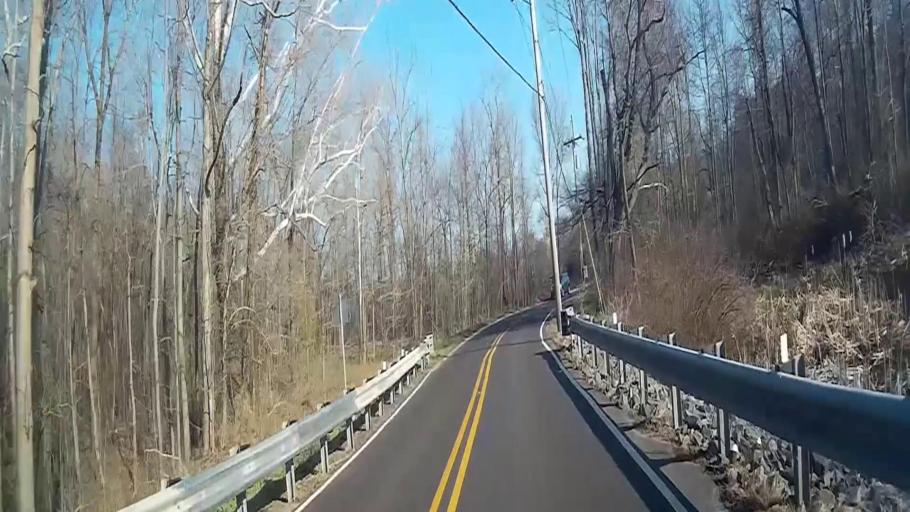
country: US
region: New Jersey
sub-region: Burlington County
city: Marlton
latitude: 39.8655
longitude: -74.8946
